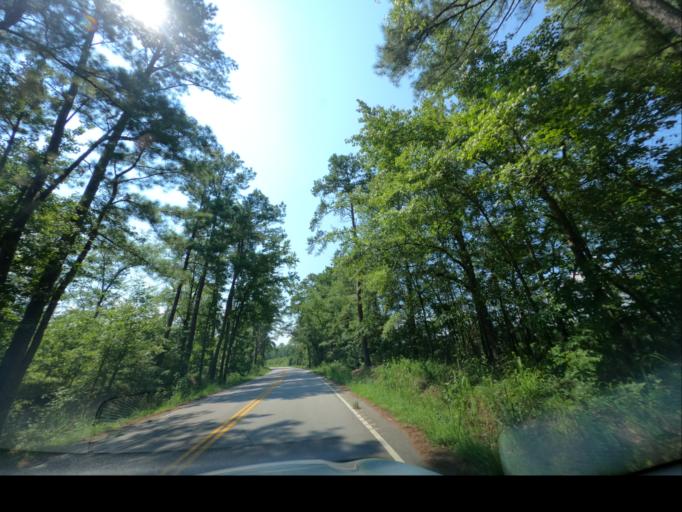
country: US
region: South Carolina
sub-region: Richland County
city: Hopkins
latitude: 33.8408
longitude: -80.8513
